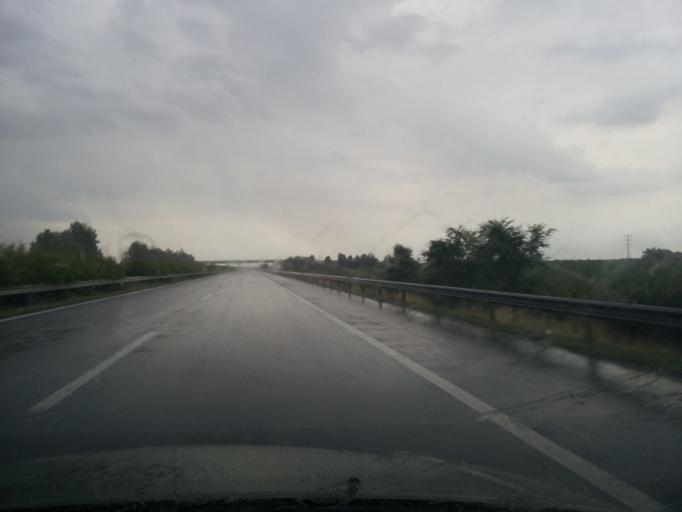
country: HU
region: Borsod-Abauj-Zemplen
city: Malyi
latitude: 48.0173
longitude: 20.8731
